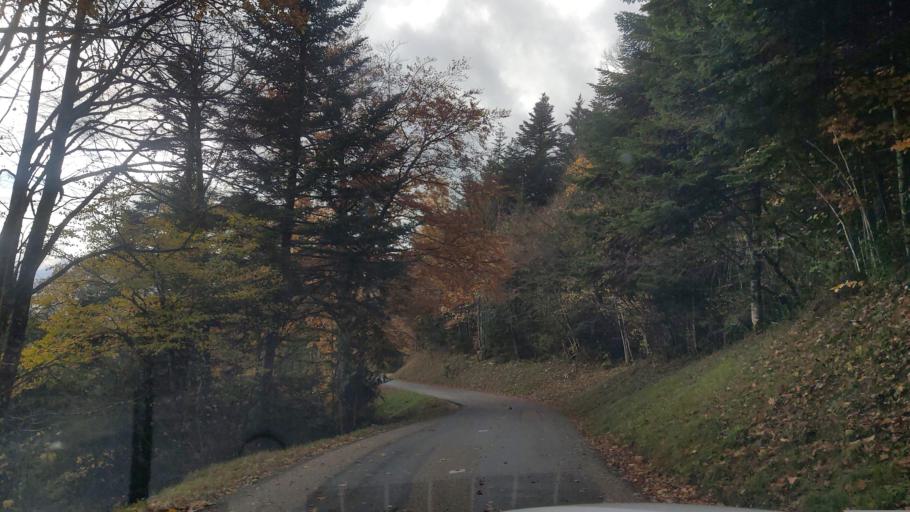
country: FR
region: Rhone-Alpes
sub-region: Departement de la Savoie
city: Le Bourget-du-Lac
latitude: 45.6552
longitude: 5.8355
